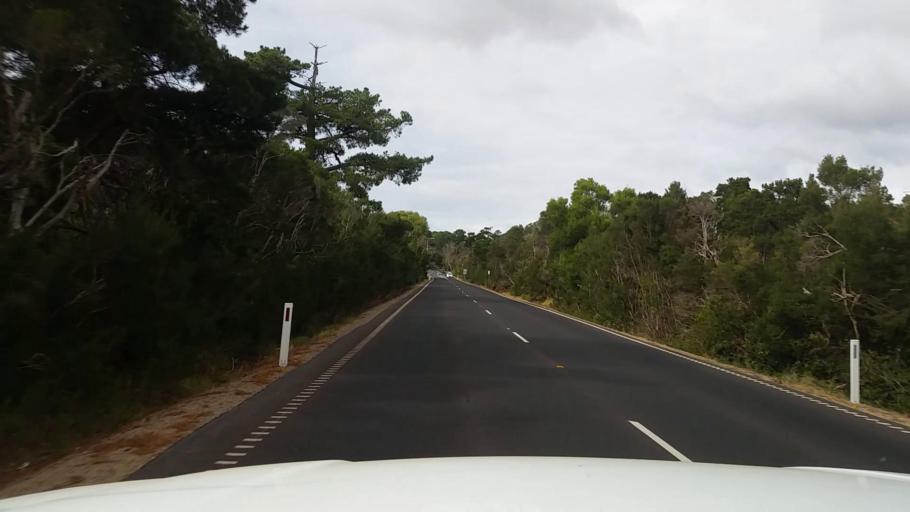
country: AU
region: Victoria
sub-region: Mornington Peninsula
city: Balnarring
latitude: -38.3606
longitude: 145.1138
